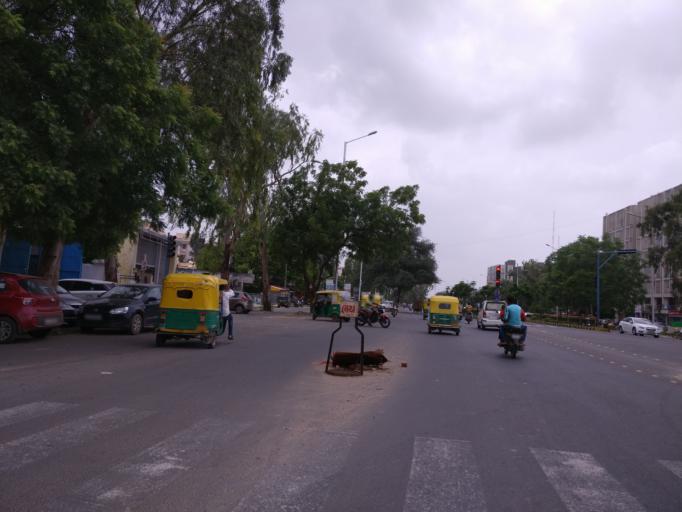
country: IN
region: Gujarat
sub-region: Gandhinagar
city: Adalaj
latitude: 23.1224
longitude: 72.5827
